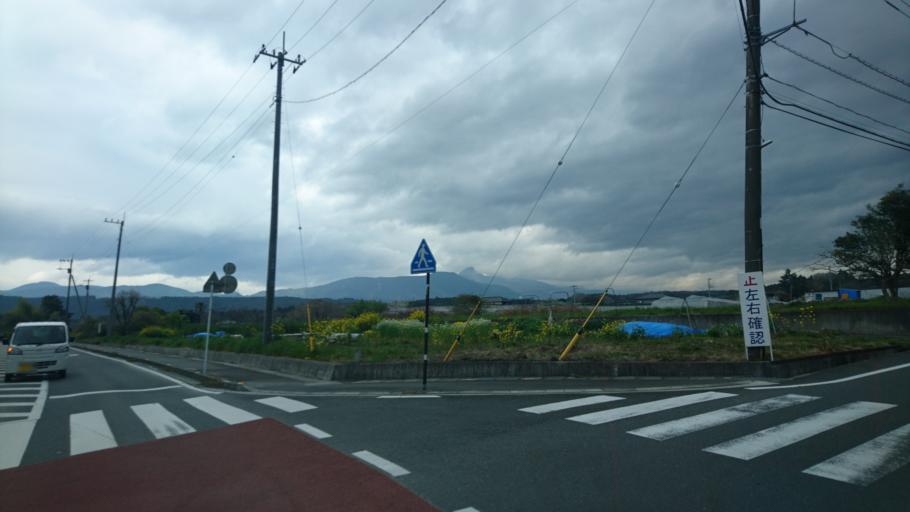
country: JP
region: Shizuoka
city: Fujinomiya
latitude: 35.2597
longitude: 138.6004
